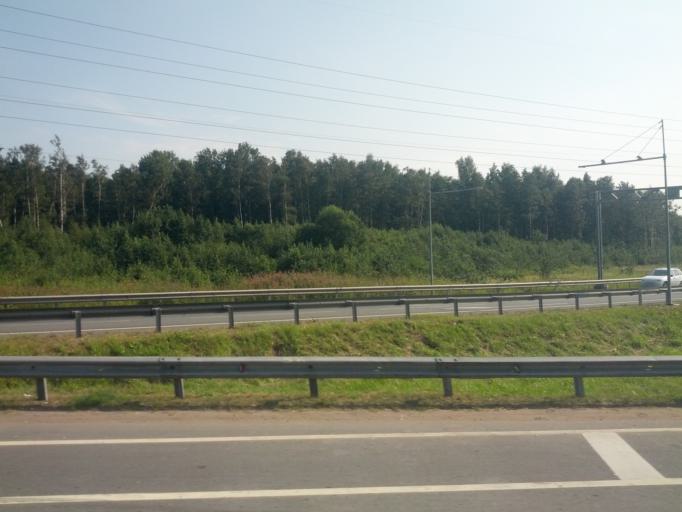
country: RU
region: Leningrad
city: Rybatskoye
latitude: 59.8928
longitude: 30.5276
